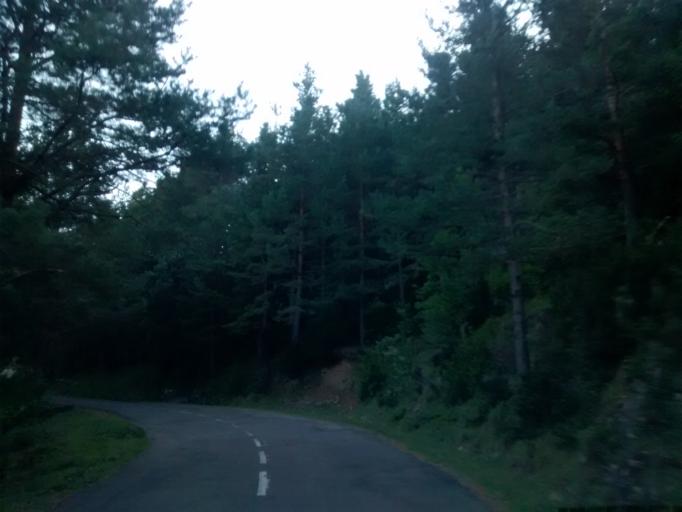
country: ES
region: Aragon
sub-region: Provincia de Huesca
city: Anso
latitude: 42.7854
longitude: -0.7380
